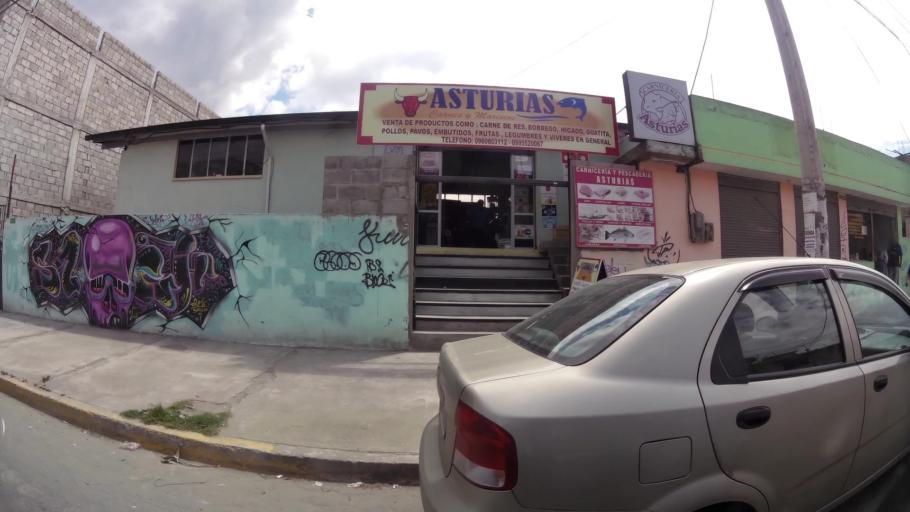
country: EC
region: Pichincha
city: Quito
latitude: -0.0699
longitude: -78.4338
